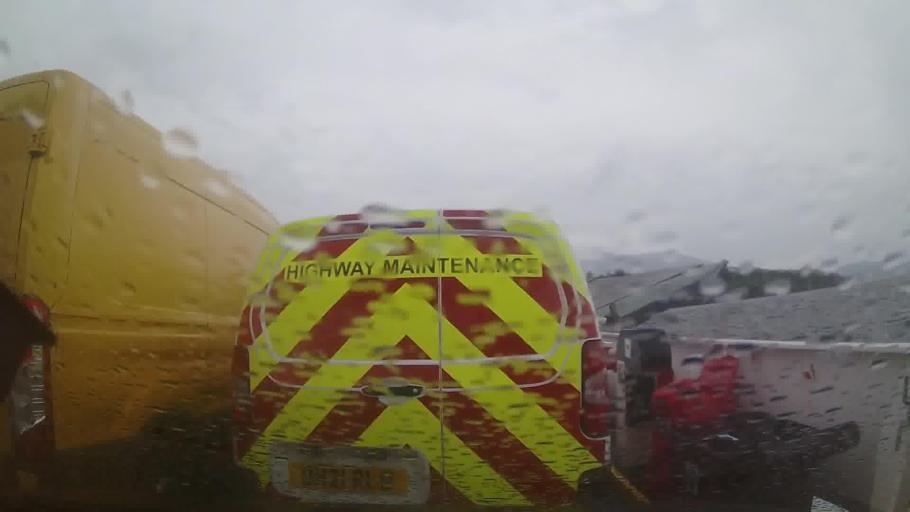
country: GB
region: Scotland
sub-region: Highland
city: Fort William
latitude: 56.7224
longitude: -5.2373
